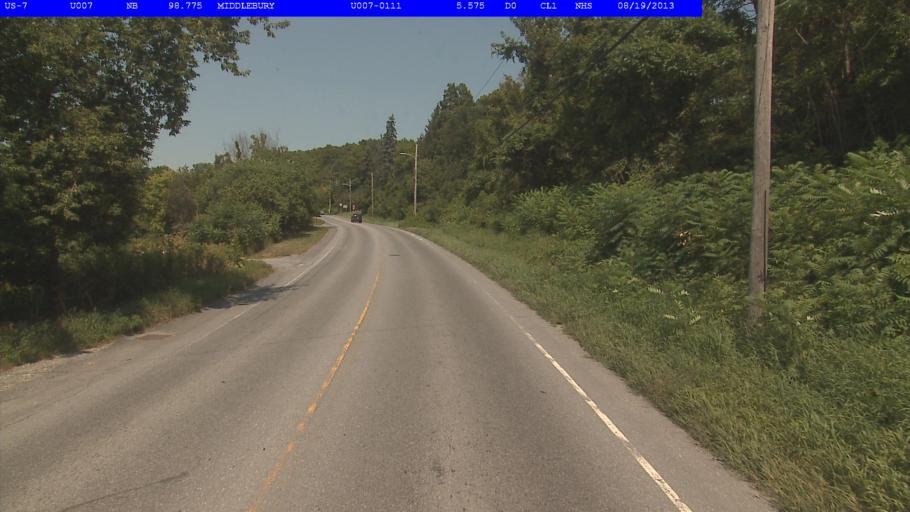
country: US
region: Vermont
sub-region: Addison County
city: Middlebury (village)
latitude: 44.0211
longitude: -73.1653
